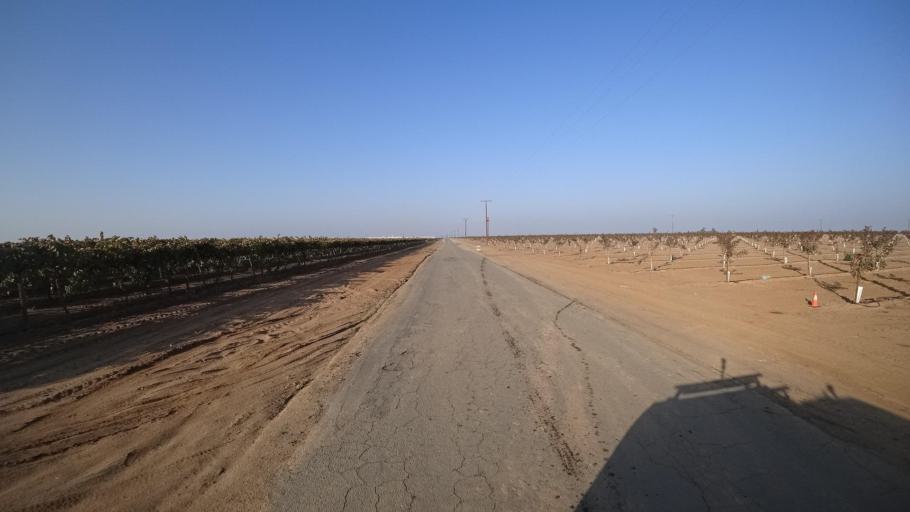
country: US
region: California
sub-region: Tulare County
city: Richgrove
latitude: 35.7763
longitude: -119.1099
